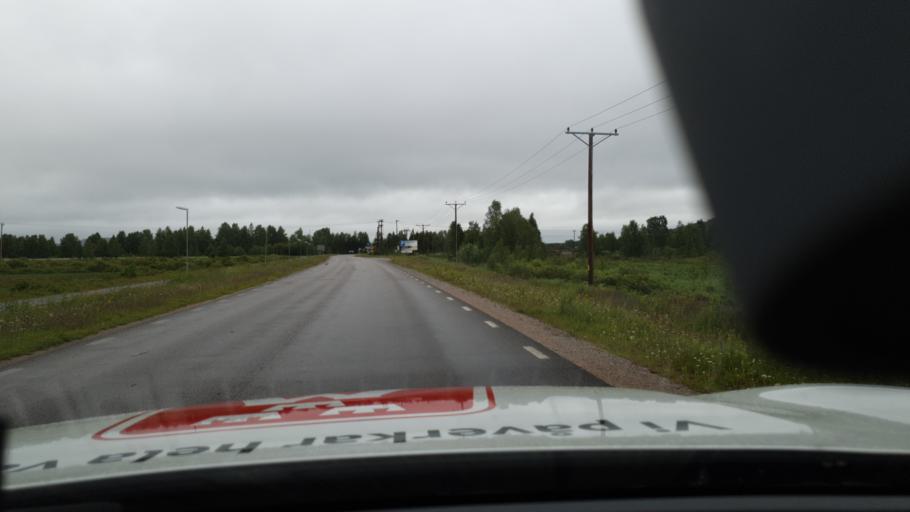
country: SE
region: Norrbotten
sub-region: Overtornea Kommun
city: OEvertornea
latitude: 66.3951
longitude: 23.6189
